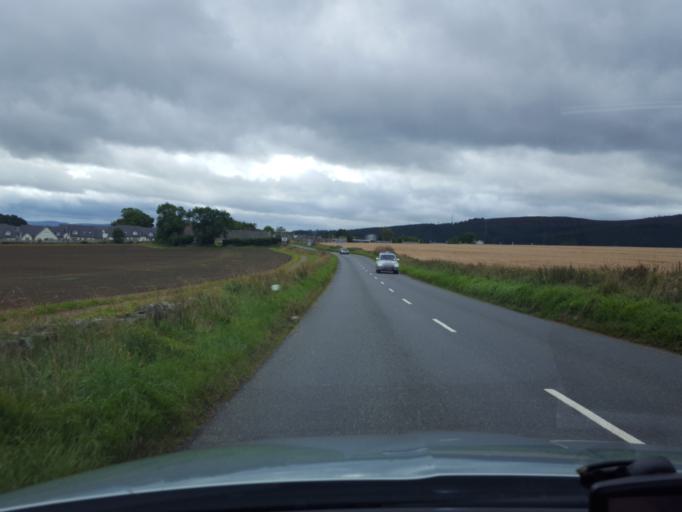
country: GB
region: Scotland
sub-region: Aberdeenshire
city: Kemnay
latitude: 57.1453
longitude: -2.4348
